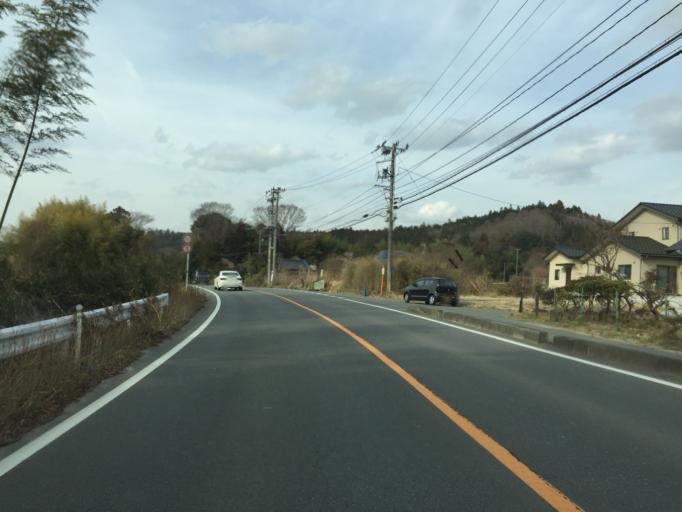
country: JP
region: Fukushima
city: Iwaki
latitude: 36.9878
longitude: 140.7379
